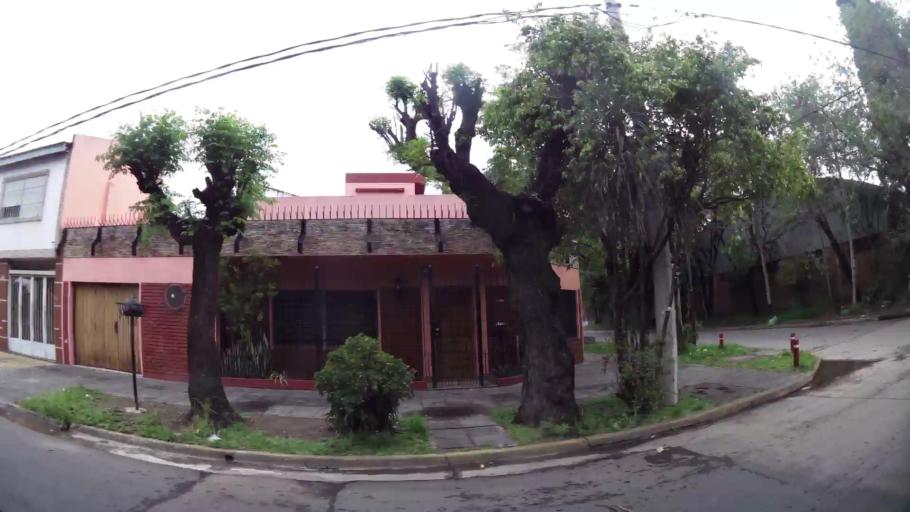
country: AR
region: Buenos Aires
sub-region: Partido de Lanus
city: Lanus
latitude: -34.7135
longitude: -58.3899
